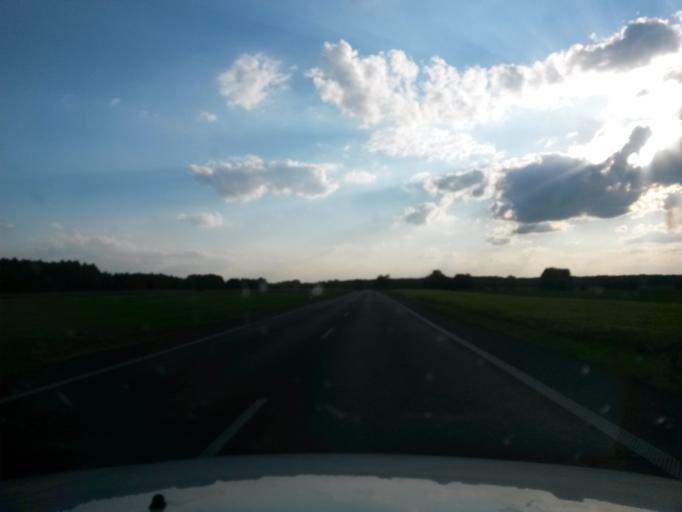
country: PL
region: Lodz Voivodeship
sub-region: Powiat belchatowski
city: Rusiec
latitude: 51.3118
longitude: 18.8956
